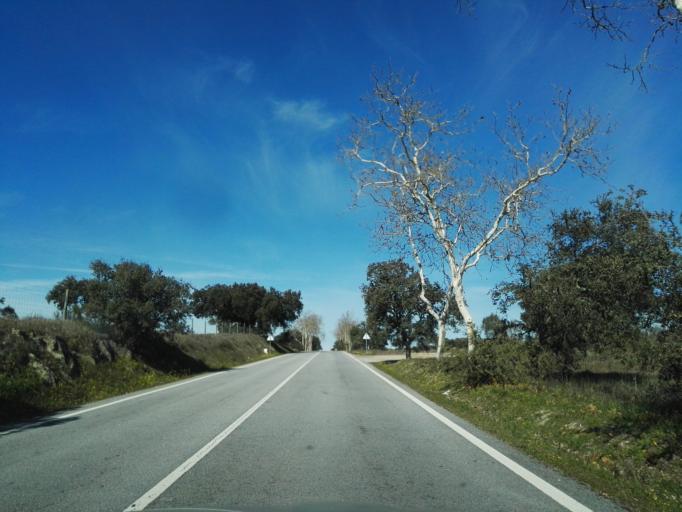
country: PT
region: Portalegre
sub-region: Arronches
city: Arronches
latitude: 39.0599
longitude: -7.2729
